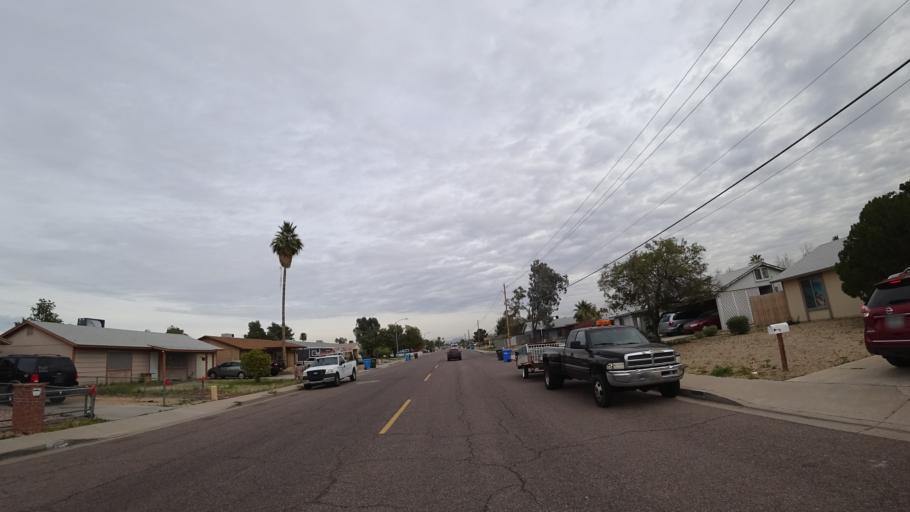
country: US
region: Arizona
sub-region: Maricopa County
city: Glendale
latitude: 33.6474
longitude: -112.1328
